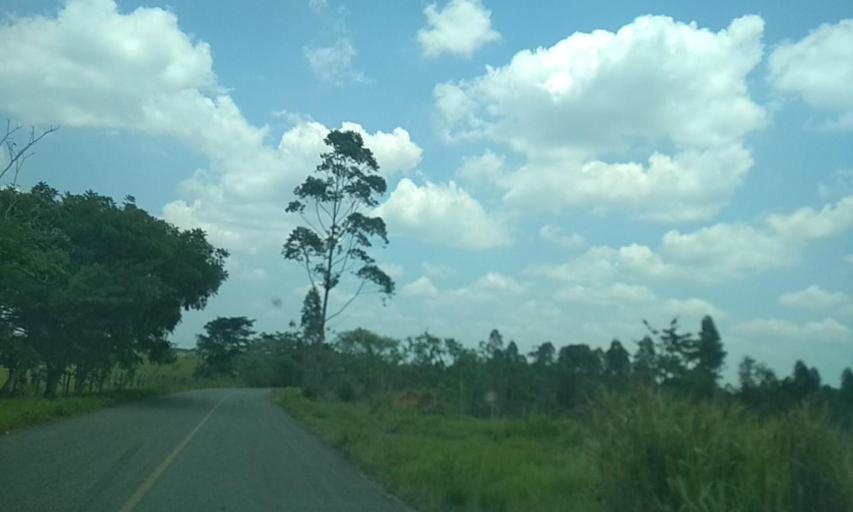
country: MX
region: Tabasco
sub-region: Huimanguillo
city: Francisco Rueda
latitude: 17.7918
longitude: -93.8457
